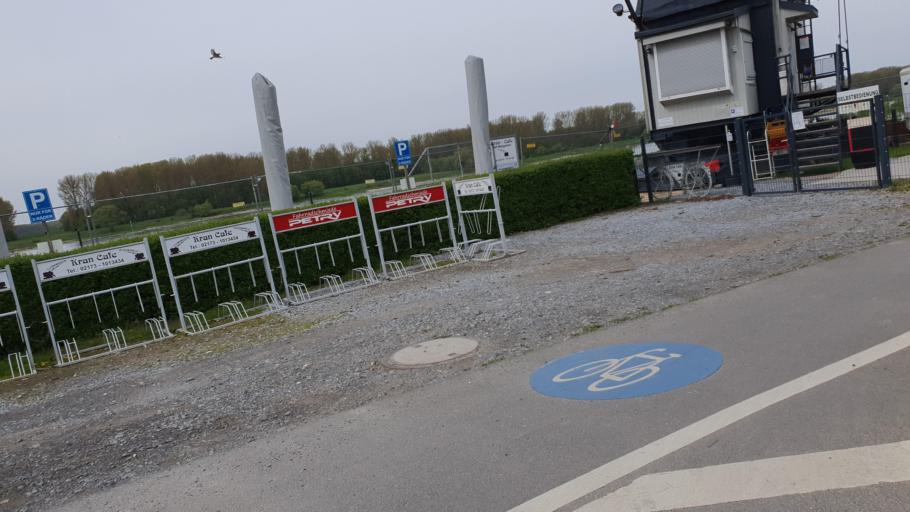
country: DE
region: North Rhine-Westphalia
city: Monheim am Rhein
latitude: 51.0618
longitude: 6.9114
